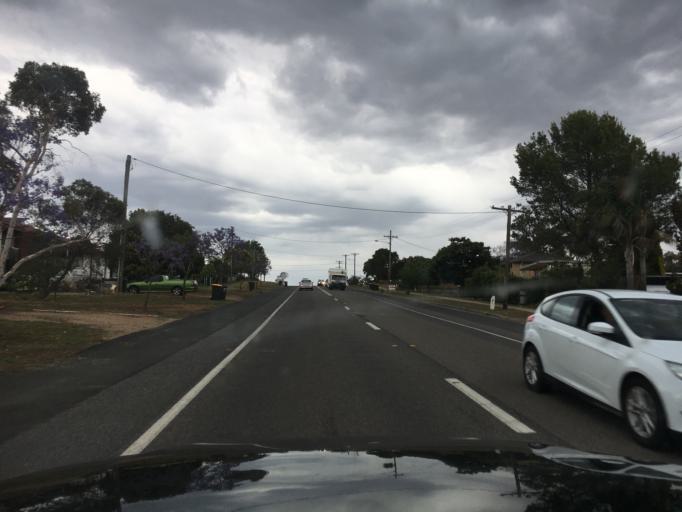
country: AU
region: New South Wales
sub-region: Muswellbrook
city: Muswellbrook
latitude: -32.1702
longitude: 150.8910
